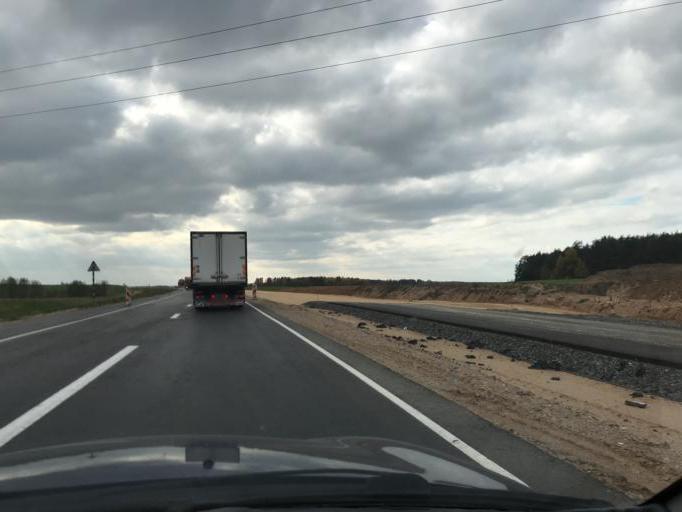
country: BY
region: Grodnenskaya
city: Lida
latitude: 53.8228
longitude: 25.1258
